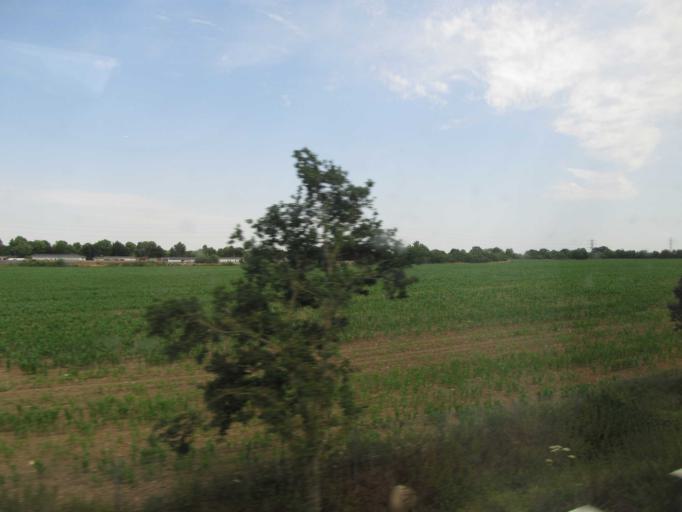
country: GB
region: England
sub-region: Surrey
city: Colnbrook
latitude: 51.5083
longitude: -0.5280
